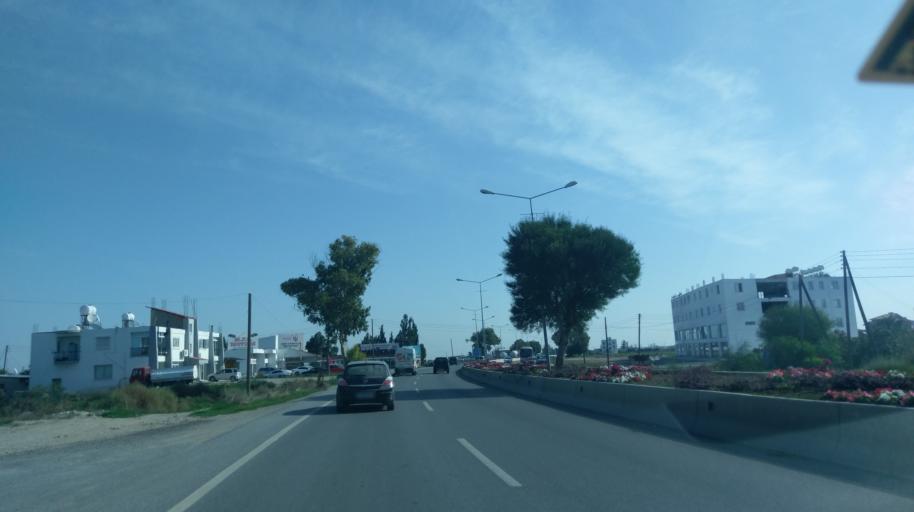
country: CY
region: Lefkosia
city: Nicosia
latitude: 35.2222
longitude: 33.4832
